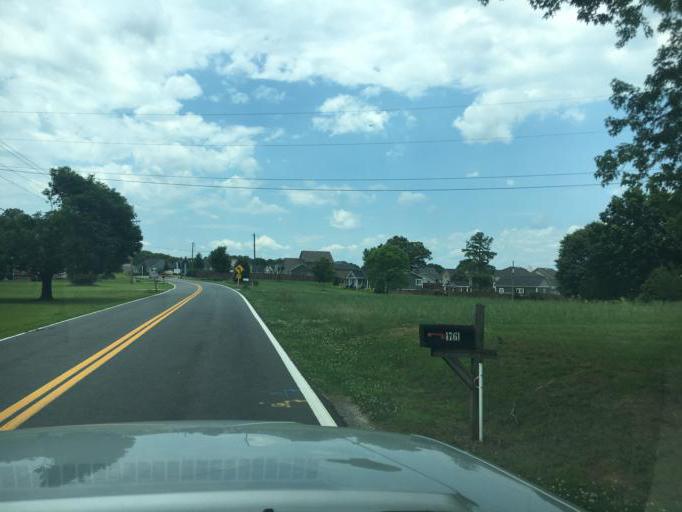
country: US
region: South Carolina
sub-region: Spartanburg County
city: Duncan
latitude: 34.8739
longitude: -82.1696
